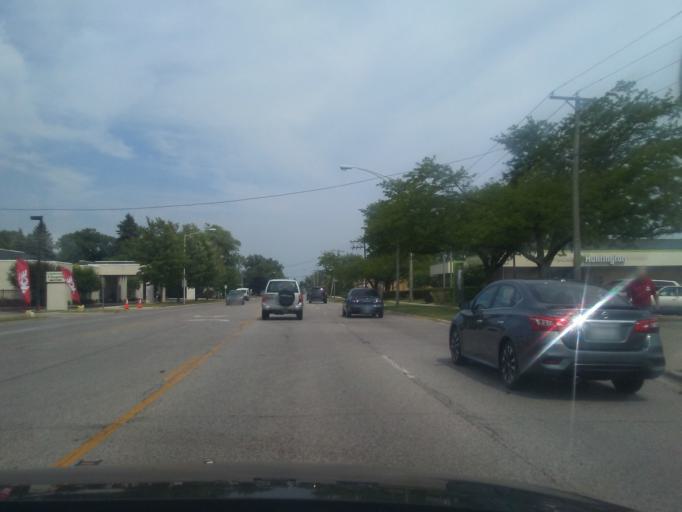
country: US
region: Illinois
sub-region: Cook County
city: Norridge
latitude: 41.9666
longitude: -87.8354
